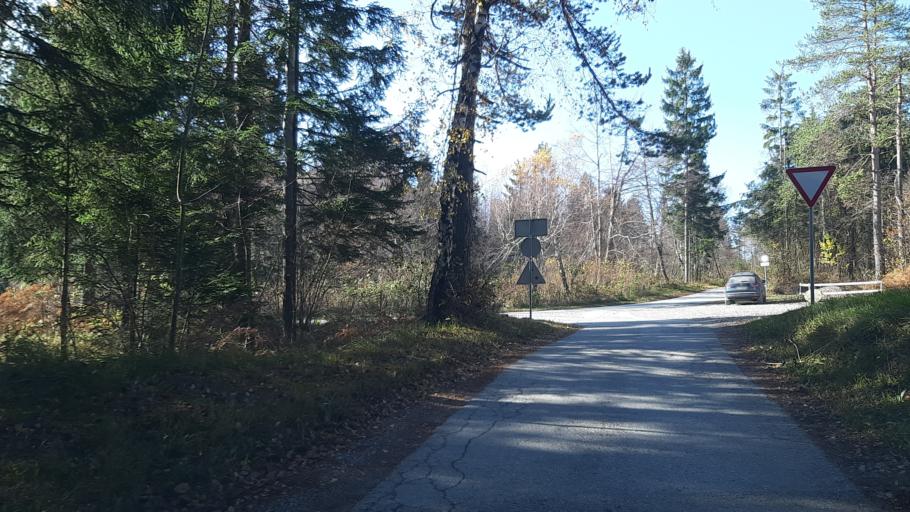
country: SI
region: Borovnica
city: Borovnica
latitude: 45.8958
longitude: 14.3541
